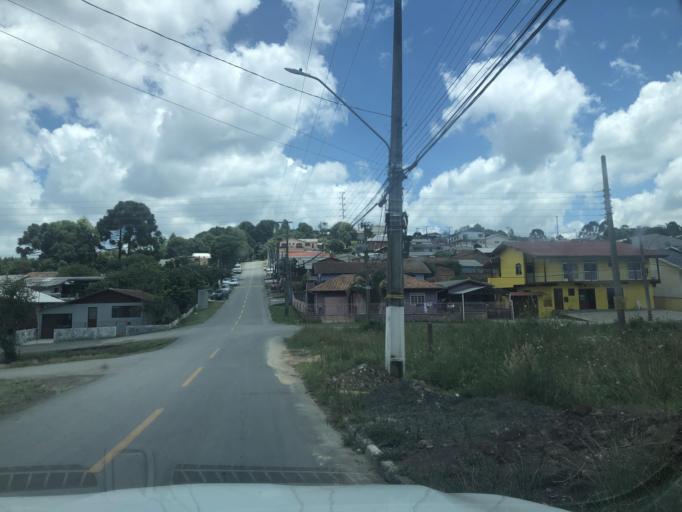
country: BR
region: Santa Catarina
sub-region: Lages
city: Lages
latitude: -27.7857
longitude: -50.3130
